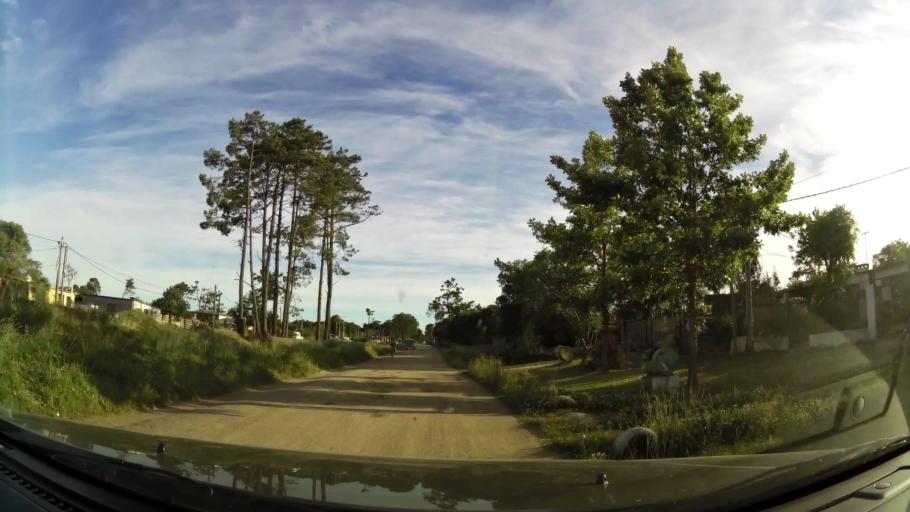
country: UY
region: Canelones
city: Empalme Olmos
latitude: -34.7751
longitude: -55.8639
